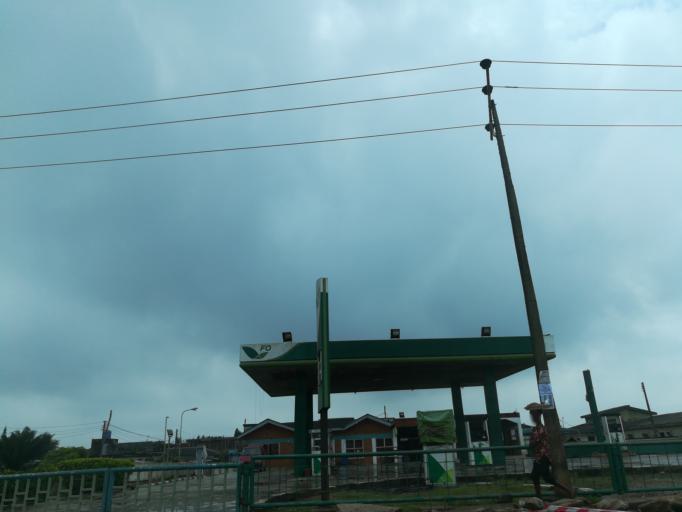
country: NG
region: Lagos
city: Ikorodu
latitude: 6.6570
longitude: 3.5196
